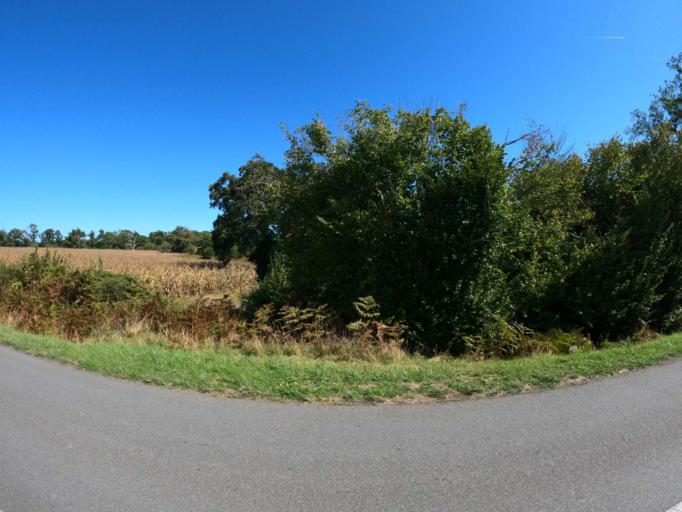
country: FR
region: Limousin
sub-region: Departement de la Haute-Vienne
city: Le Dorat
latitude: 46.2358
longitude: 1.0577
